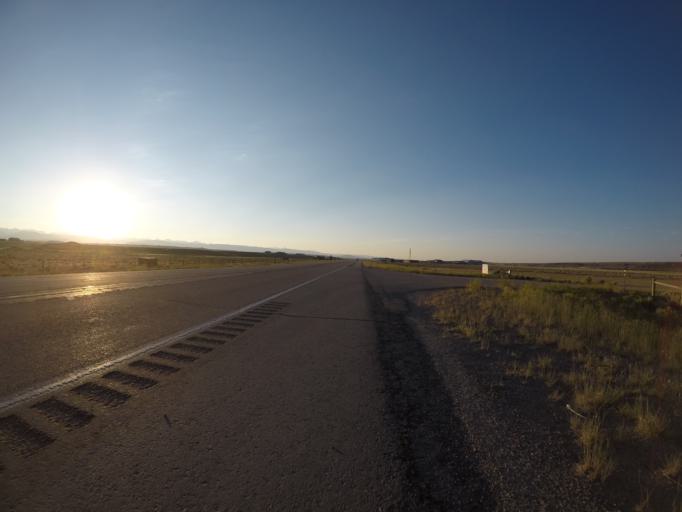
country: US
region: Wyoming
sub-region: Sublette County
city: Pinedale
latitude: 42.8020
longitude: -109.8125
